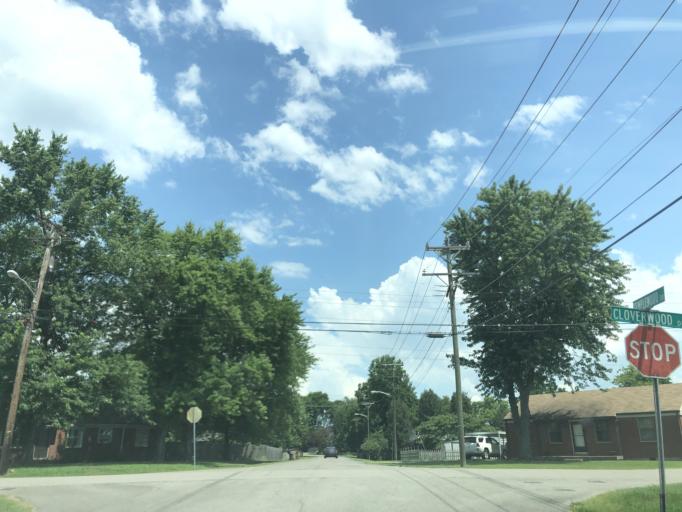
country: US
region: Tennessee
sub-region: Davidson County
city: Lakewood
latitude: 36.1568
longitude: -86.6498
